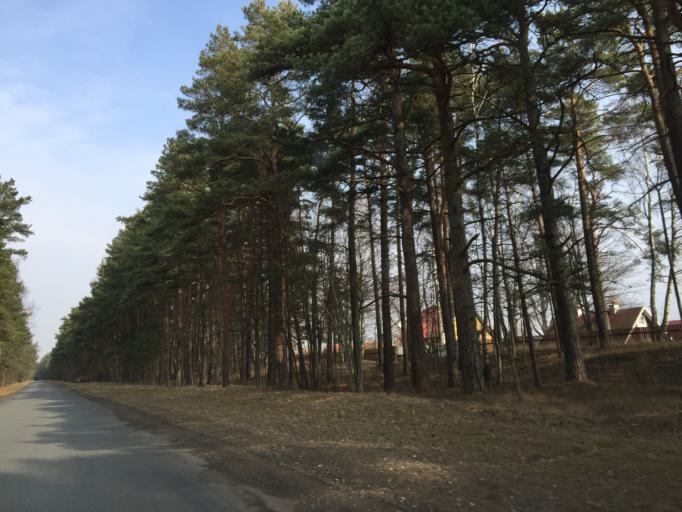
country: LV
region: Salacgrivas
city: Ainazi
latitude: 57.8927
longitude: 24.3711
